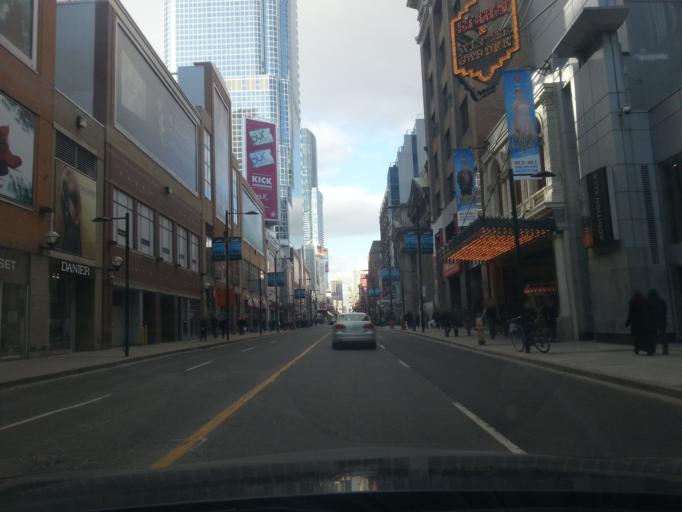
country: CA
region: Ontario
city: Toronto
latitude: 43.6528
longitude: -79.3794
